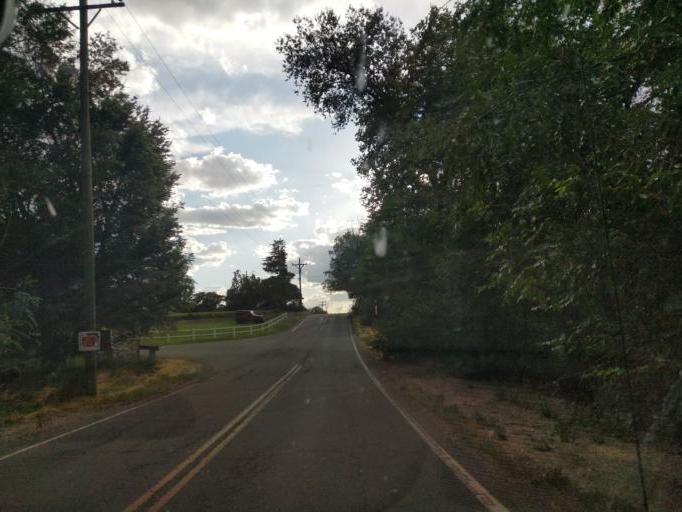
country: US
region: Colorado
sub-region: Mesa County
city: Clifton
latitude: 39.0559
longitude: -108.4264
